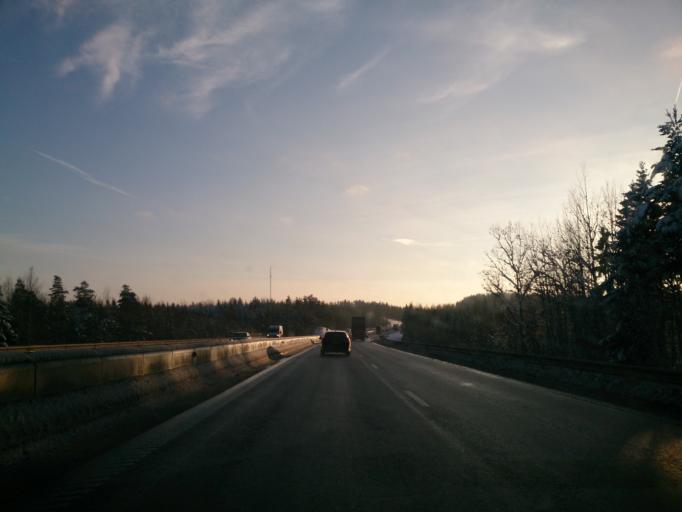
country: SE
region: OEstergoetland
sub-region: Norrkopings Kommun
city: Kimstad
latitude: 58.5083
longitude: 15.9910
